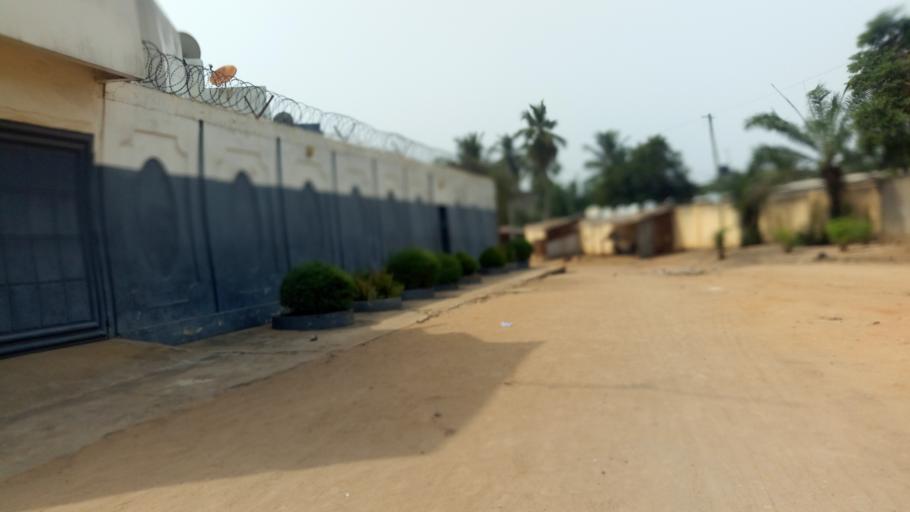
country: TG
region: Maritime
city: Lome
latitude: 6.1753
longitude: 1.1729
